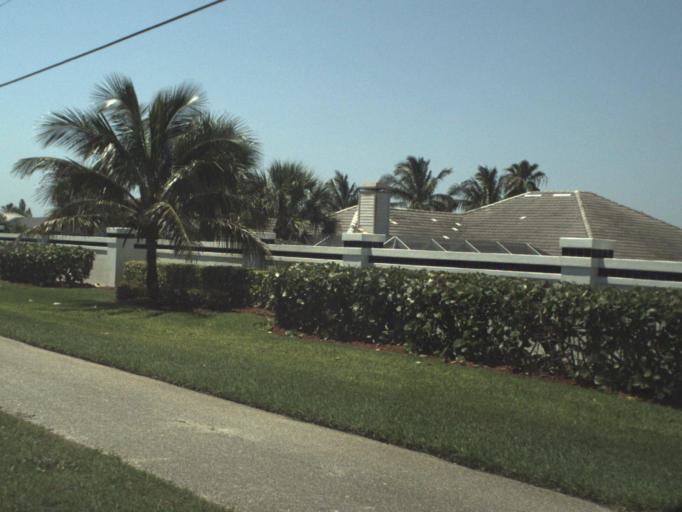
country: US
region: Florida
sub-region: Brevard County
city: Malabar
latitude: 27.9904
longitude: -80.5200
